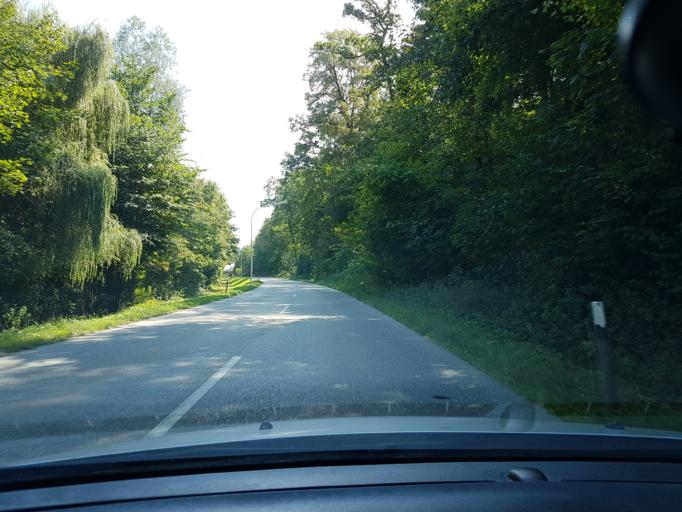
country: DE
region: Bavaria
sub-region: Upper Bavaria
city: Altoetting
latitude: 48.2412
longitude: 12.6713
